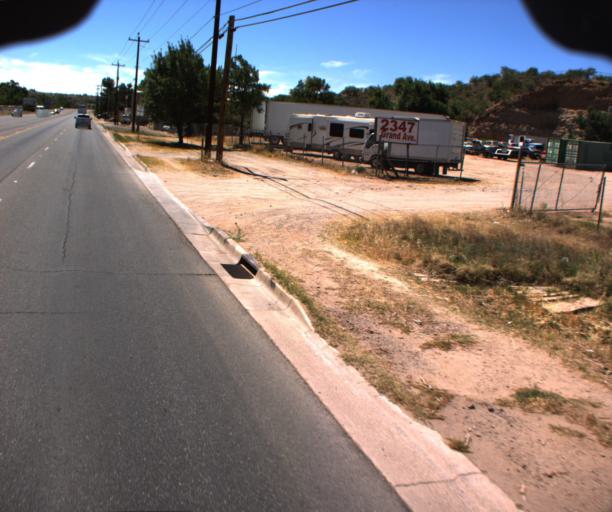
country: US
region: Arizona
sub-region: Santa Cruz County
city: Nogales
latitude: 31.3754
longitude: -110.9370
